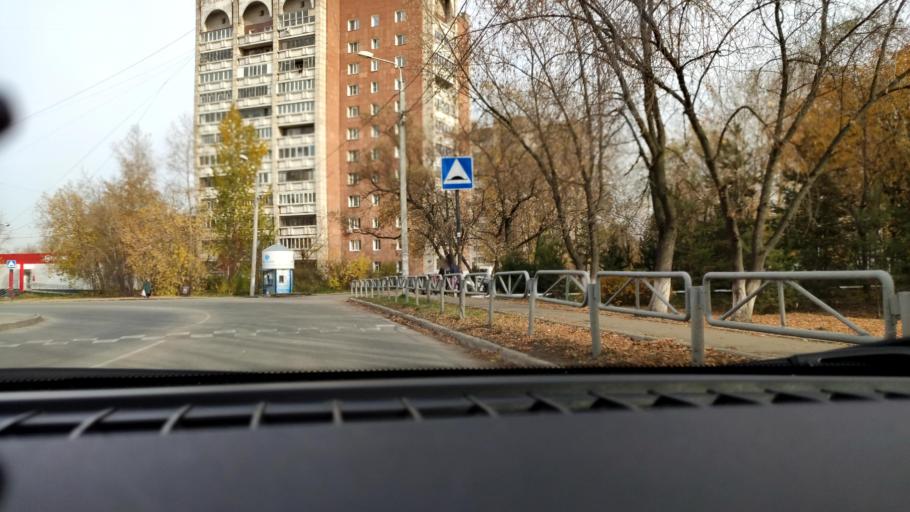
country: RU
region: Perm
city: Perm
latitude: 58.0666
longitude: 56.3561
